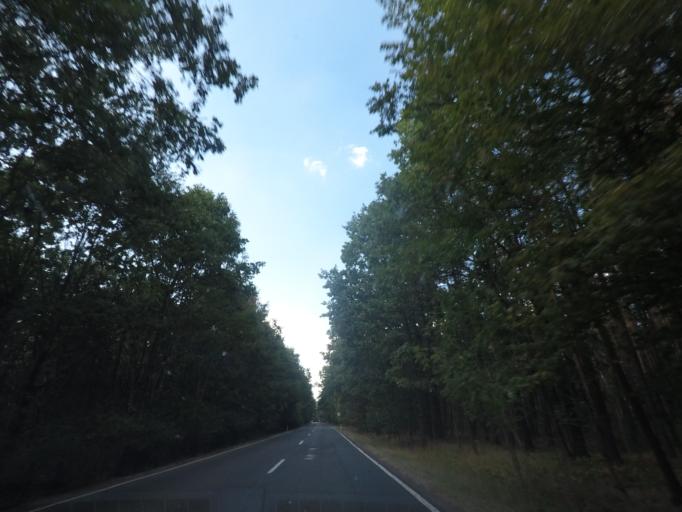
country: CZ
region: Kralovehradecky
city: Dolni Cernilov
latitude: 50.3092
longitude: 15.9521
